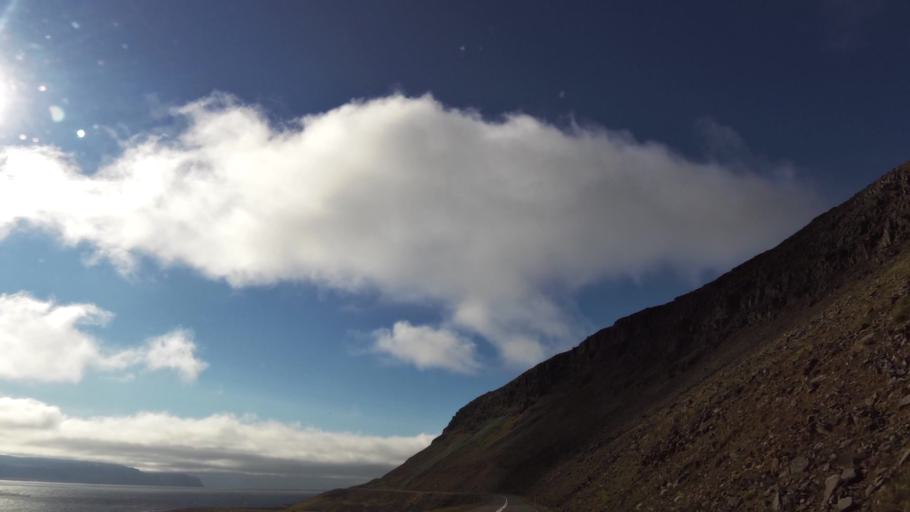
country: IS
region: West
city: Olafsvik
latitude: 65.5776
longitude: -23.9466
